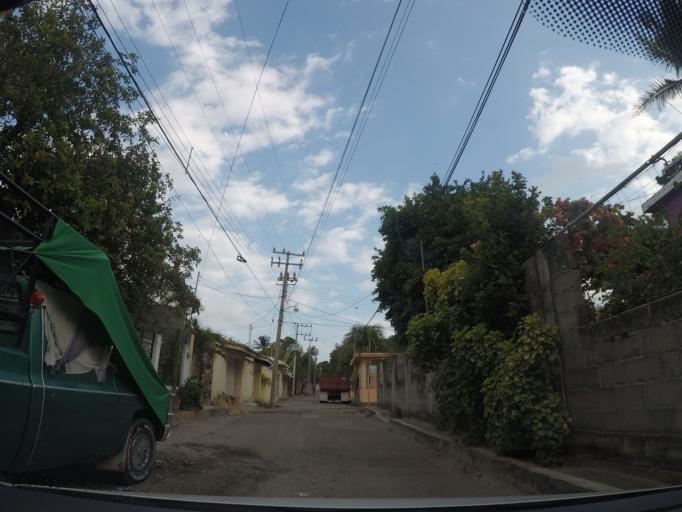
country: MX
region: Oaxaca
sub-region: Salina Cruz
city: Salina Cruz
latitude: 16.2086
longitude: -95.2074
